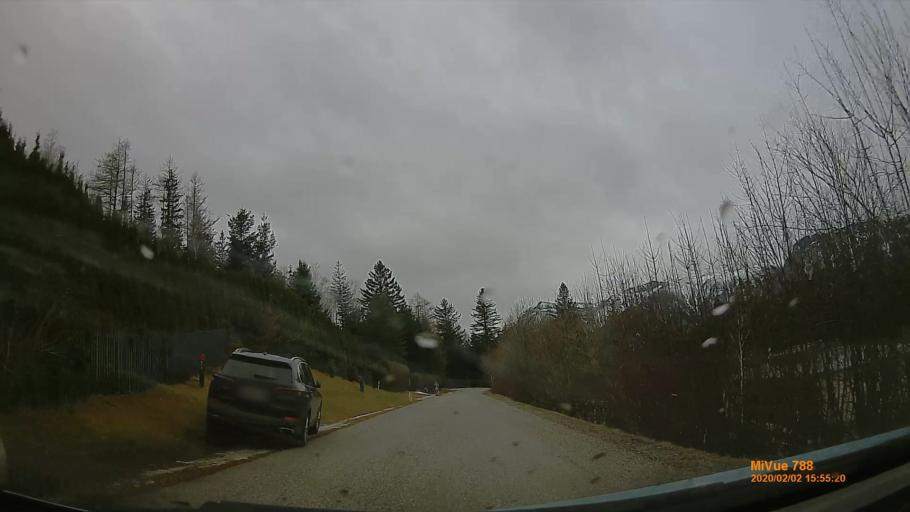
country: AT
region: Lower Austria
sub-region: Politischer Bezirk Neunkirchen
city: Semmering
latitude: 47.6702
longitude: 15.7880
